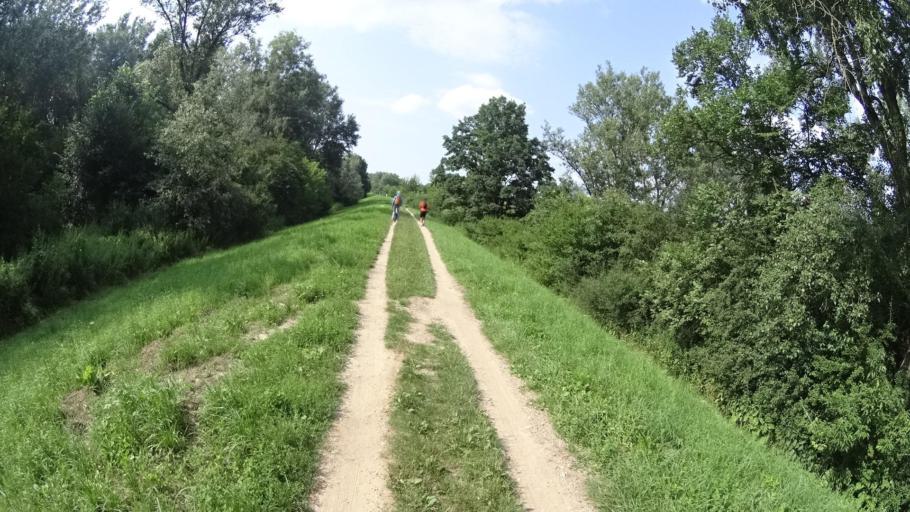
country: PL
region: Masovian Voivodeship
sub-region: Powiat legionowski
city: Jablonna
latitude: 52.3644
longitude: 20.9184
